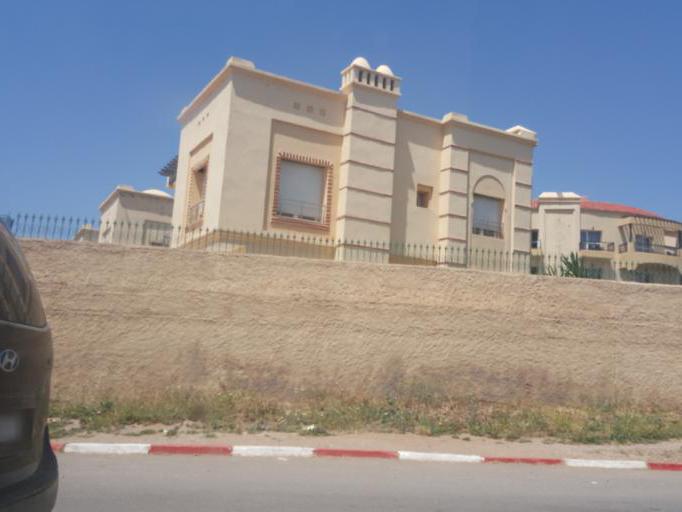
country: MA
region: Fes-Boulemane
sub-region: Fes
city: Fes
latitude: 34.0469
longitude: -5.0374
